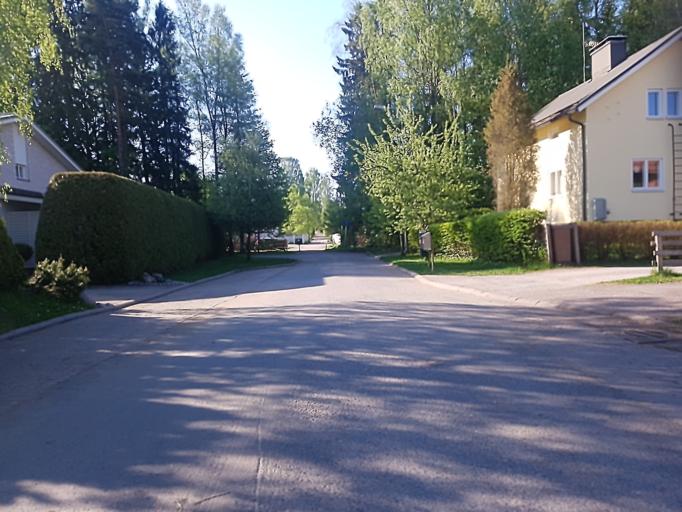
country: FI
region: Uusimaa
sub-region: Helsinki
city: Helsinki
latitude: 60.2478
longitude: 24.9311
